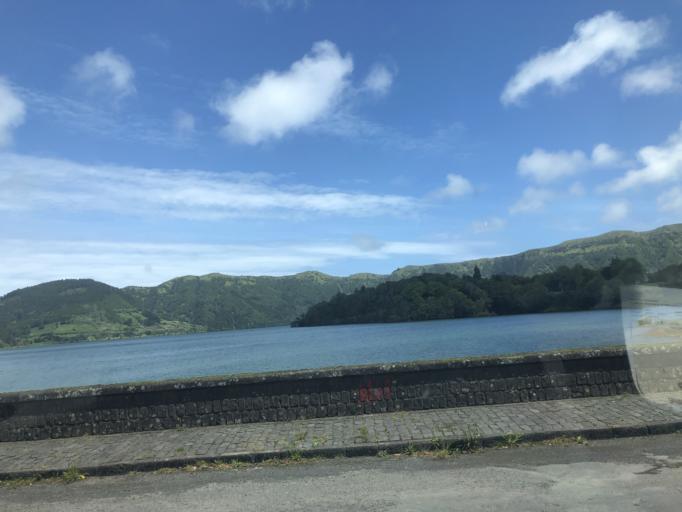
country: PT
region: Azores
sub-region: Ponta Delgada
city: Arrifes
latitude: 37.8549
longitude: -25.7854
